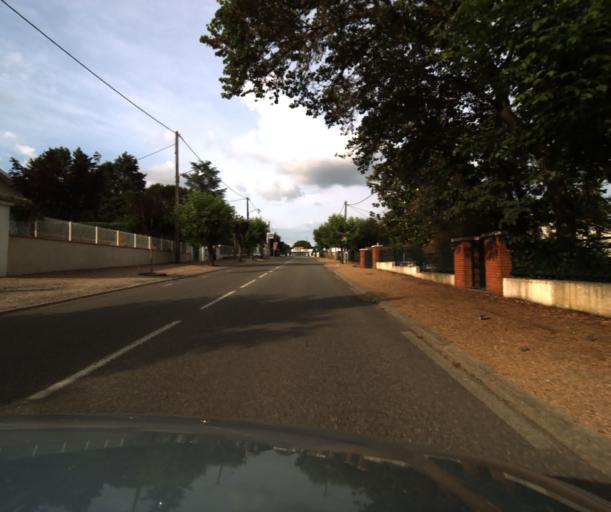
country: FR
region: Midi-Pyrenees
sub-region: Departement du Tarn-et-Garonne
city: Beaumont-de-Lomagne
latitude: 43.8793
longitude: 0.9822
